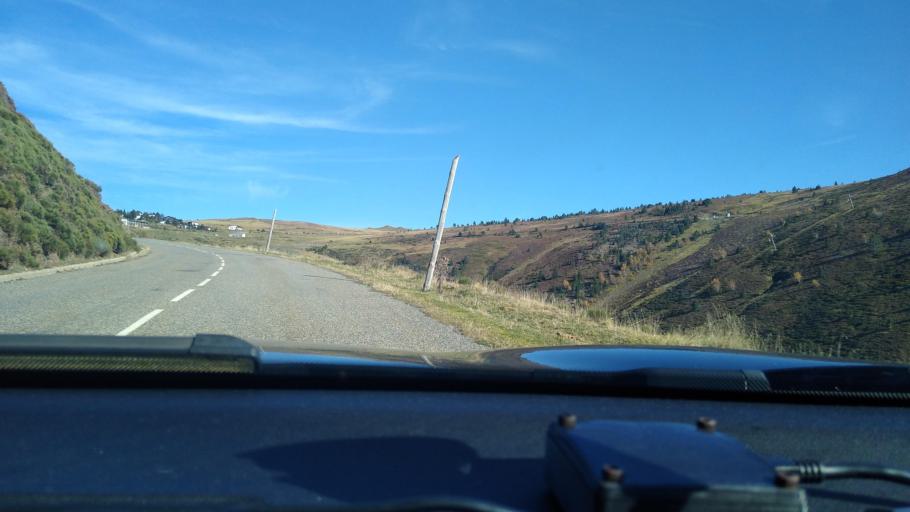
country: FR
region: Midi-Pyrenees
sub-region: Departement de l'Ariege
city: Ax-les-Thermes
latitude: 42.7313
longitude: 1.9754
